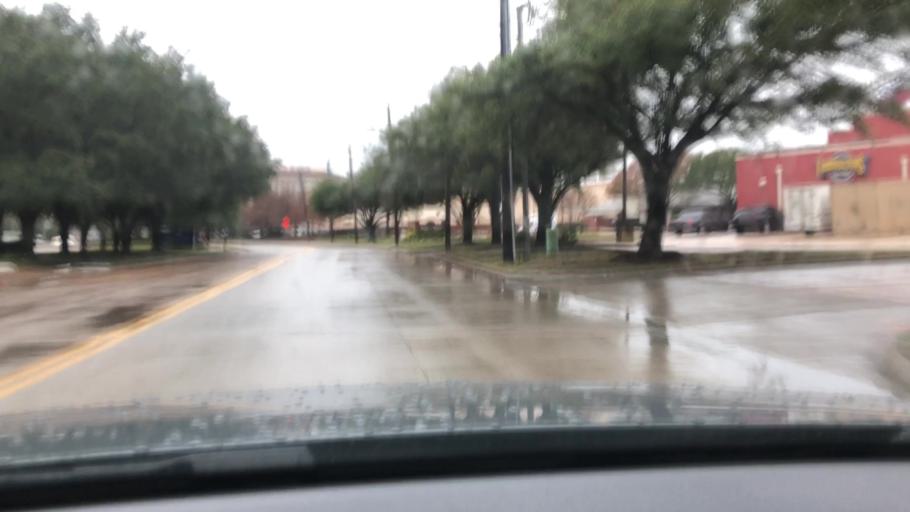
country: US
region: Texas
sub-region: Harris County
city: Bunker Hill Village
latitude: 29.7816
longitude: -95.5561
